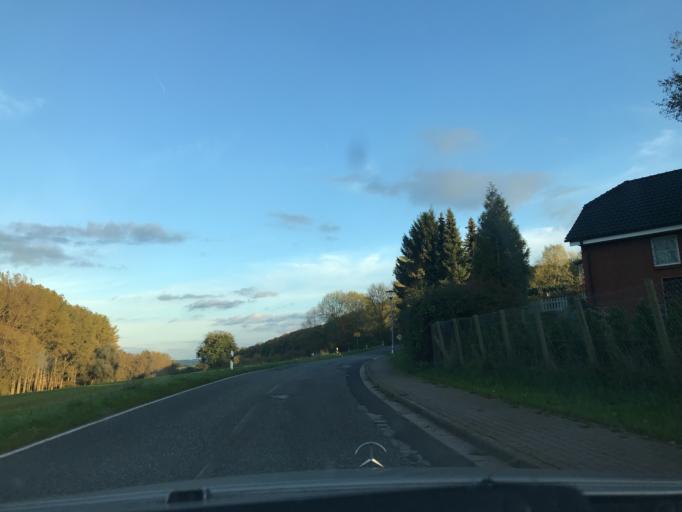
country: DE
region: Hesse
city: Witzenhausen
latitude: 51.4041
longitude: 9.8637
